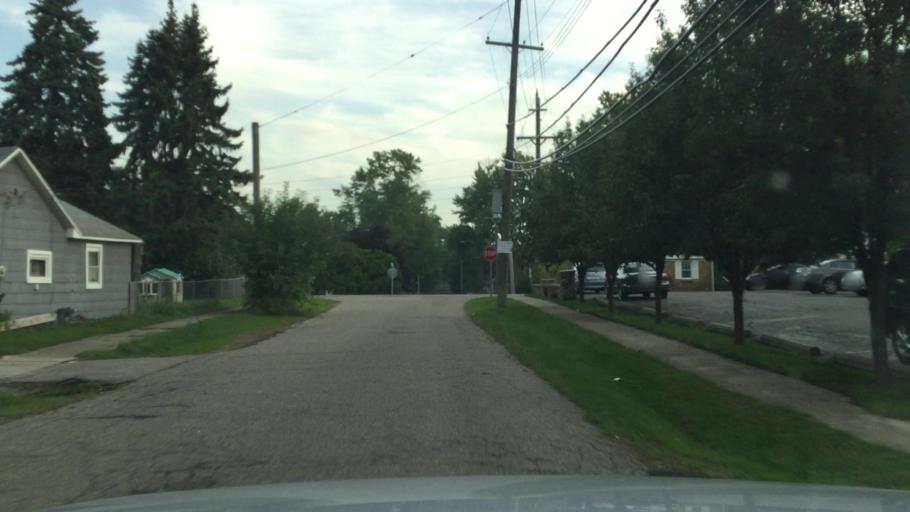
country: US
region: Michigan
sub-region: Oakland County
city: Sylvan Lake
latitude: 42.6307
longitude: -83.3322
